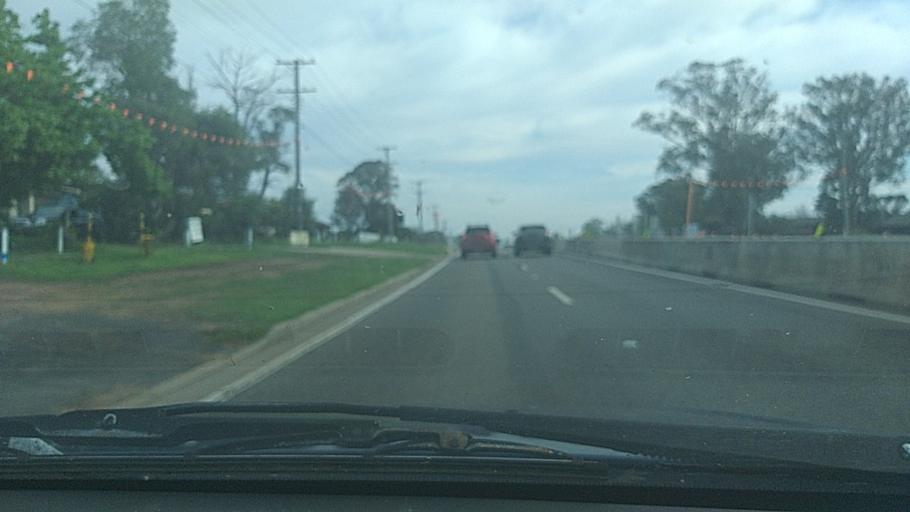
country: AU
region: New South Wales
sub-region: Penrith Municipality
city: Kingswood Park
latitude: -33.7709
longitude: 150.7110
